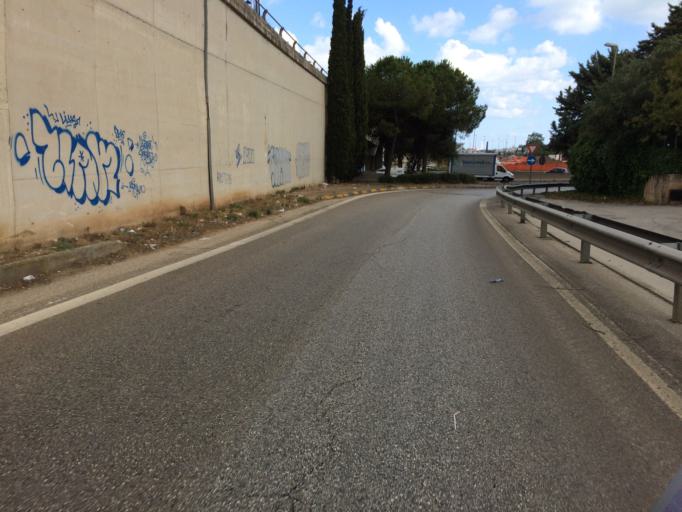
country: IT
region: Apulia
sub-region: Provincia di Bari
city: Bari
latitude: 41.0954
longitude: 16.8290
